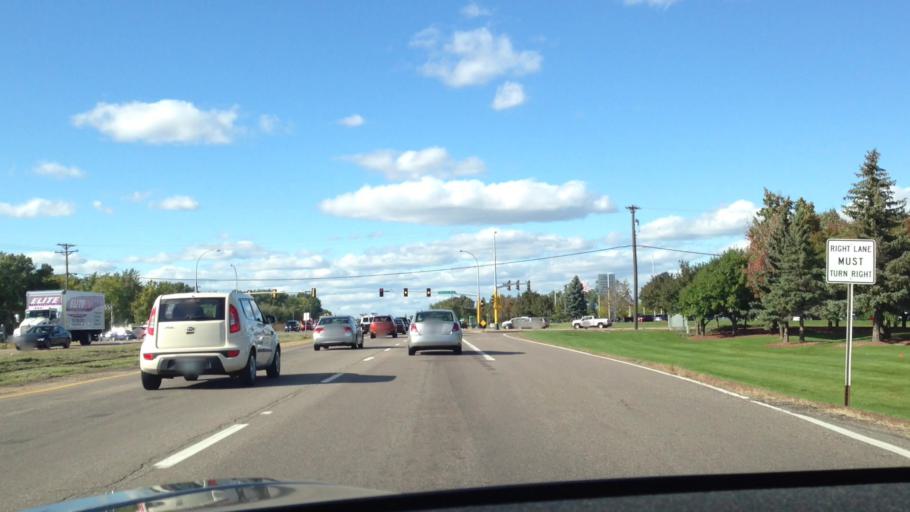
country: US
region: Minnesota
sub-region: Hennepin County
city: Brooklyn Park
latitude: 45.0936
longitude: -93.3834
